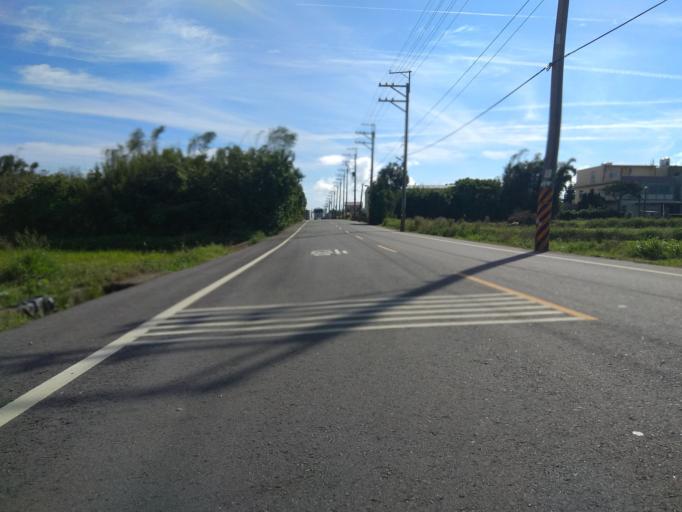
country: TW
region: Taiwan
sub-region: Hsinchu
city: Zhubei
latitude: 25.0098
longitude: 121.0409
